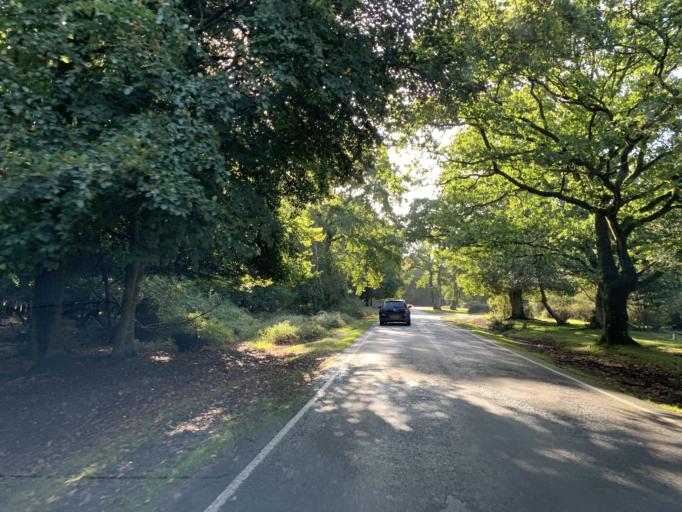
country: GB
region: England
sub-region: Hampshire
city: Cadnam
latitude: 50.9280
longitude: -1.6551
